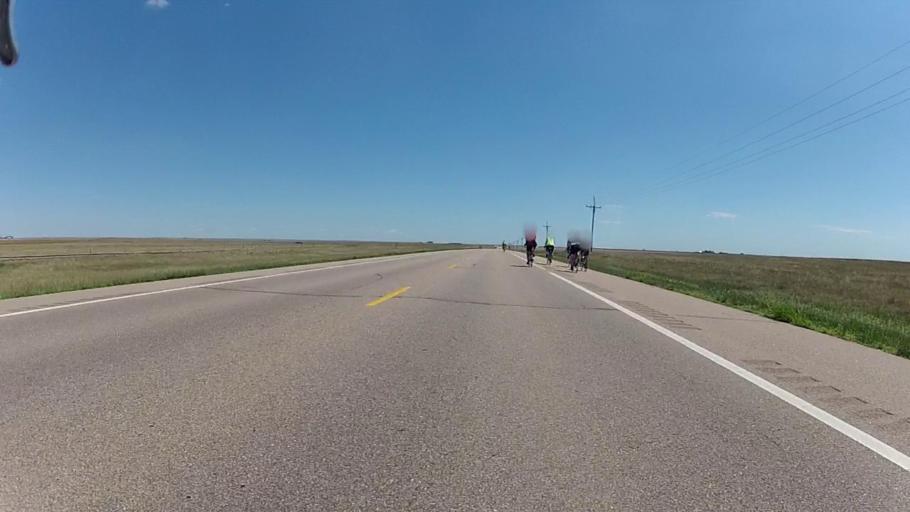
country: US
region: Kansas
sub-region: Ford County
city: Dodge City
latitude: 37.6792
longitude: -100.1848
